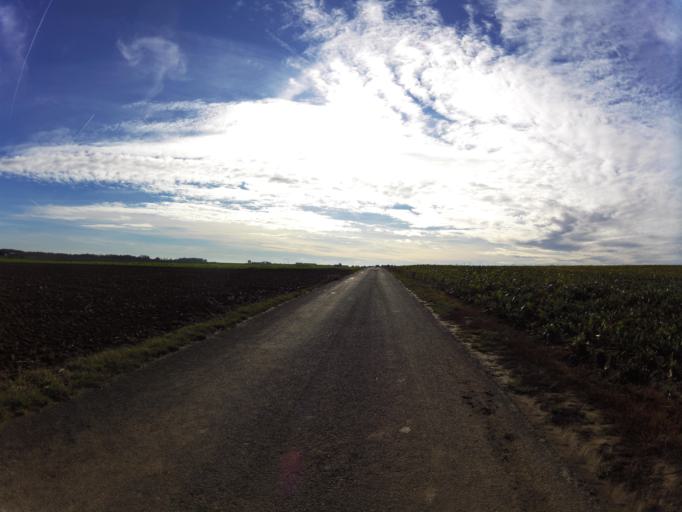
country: DE
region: Bavaria
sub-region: Regierungsbezirk Unterfranken
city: Giebelstadt
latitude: 49.6681
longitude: 9.9514
